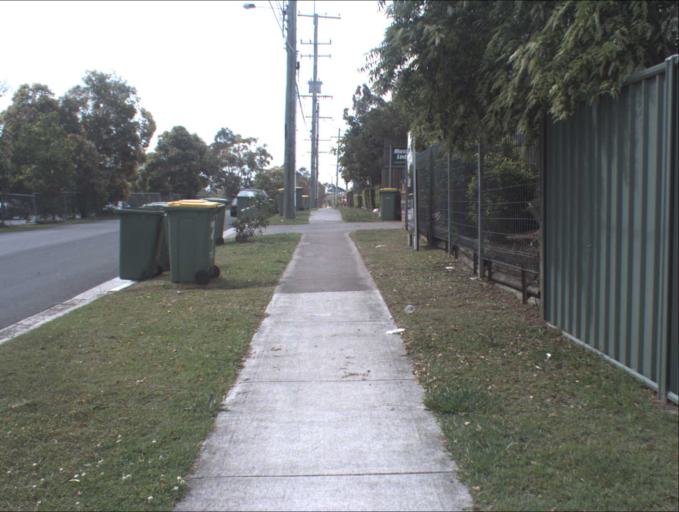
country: AU
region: Queensland
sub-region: Logan
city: Waterford West
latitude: -27.6732
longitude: 153.1223
